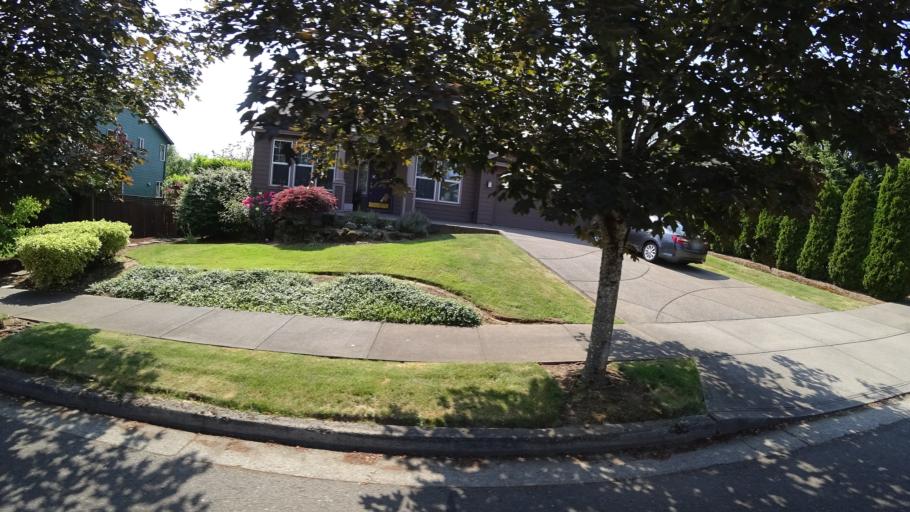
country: US
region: Oregon
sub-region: Clackamas County
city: Happy Valley
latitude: 45.4419
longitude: -122.5353
